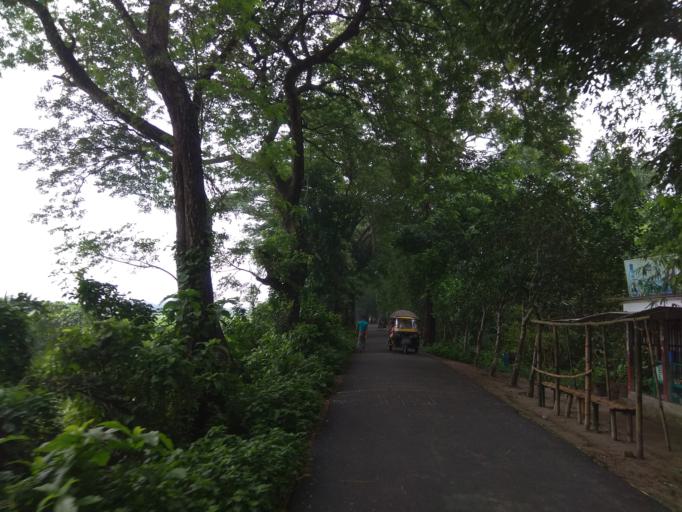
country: BD
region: Dhaka
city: Dohar
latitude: 23.4733
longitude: 90.0643
